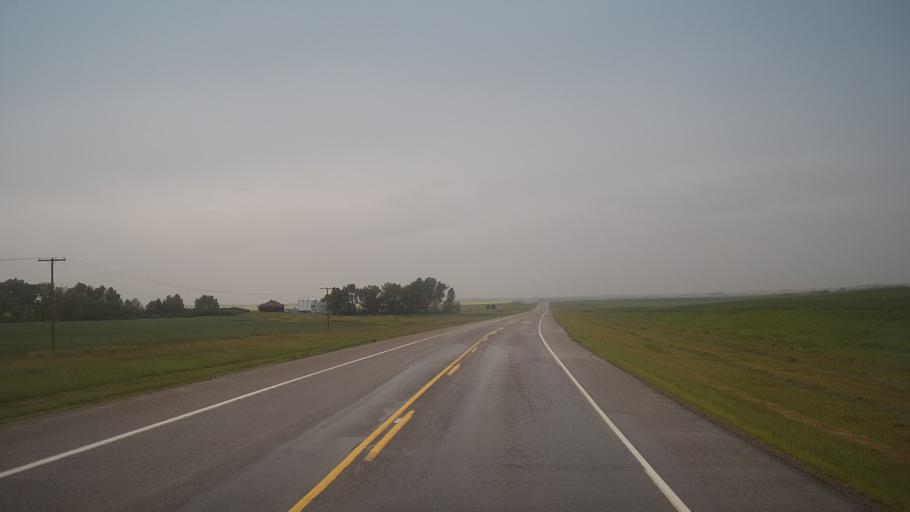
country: CA
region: Saskatchewan
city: Wilkie
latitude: 52.2035
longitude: -108.4740
